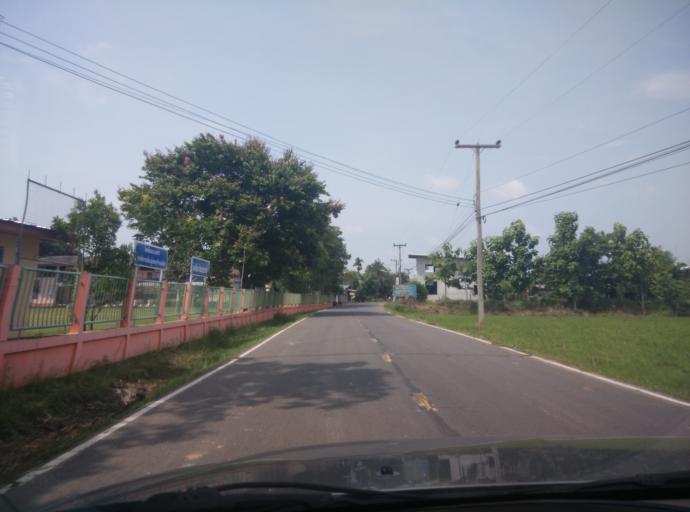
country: TH
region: Sisaket
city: Huai Thap Than
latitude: 14.9853
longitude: 104.0711
